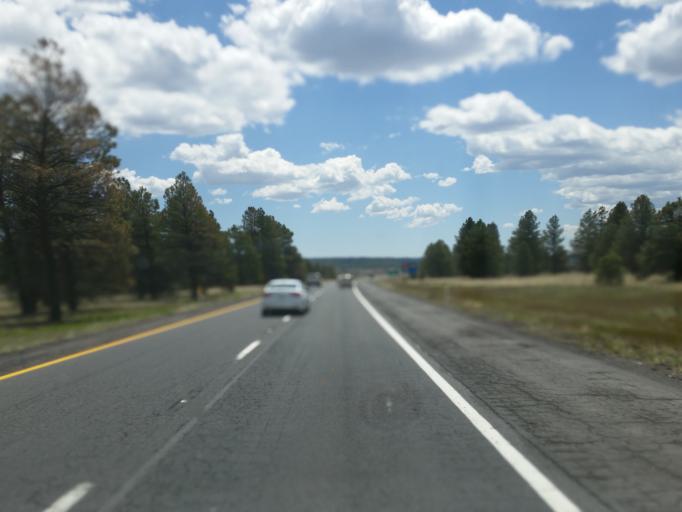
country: US
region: Arizona
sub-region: Coconino County
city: Parks
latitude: 35.2456
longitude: -111.8447
